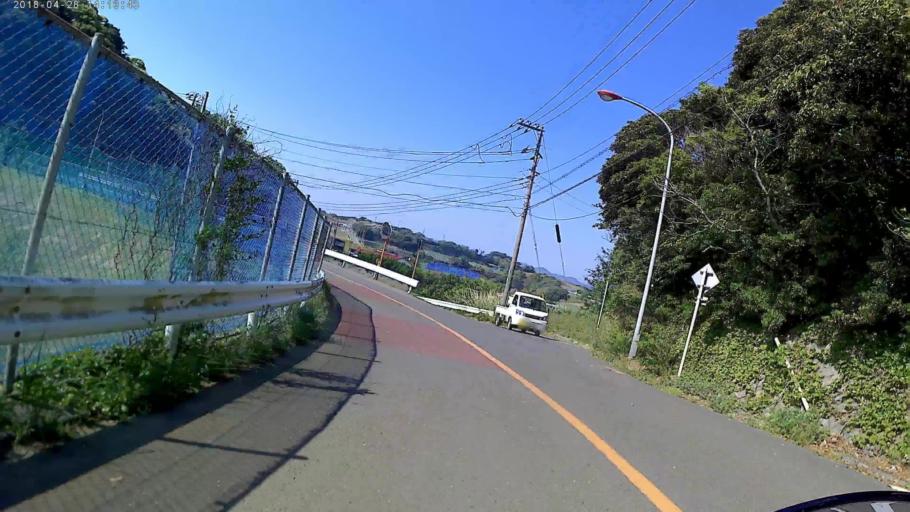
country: JP
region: Kanagawa
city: Miura
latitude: 35.1511
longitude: 139.6466
